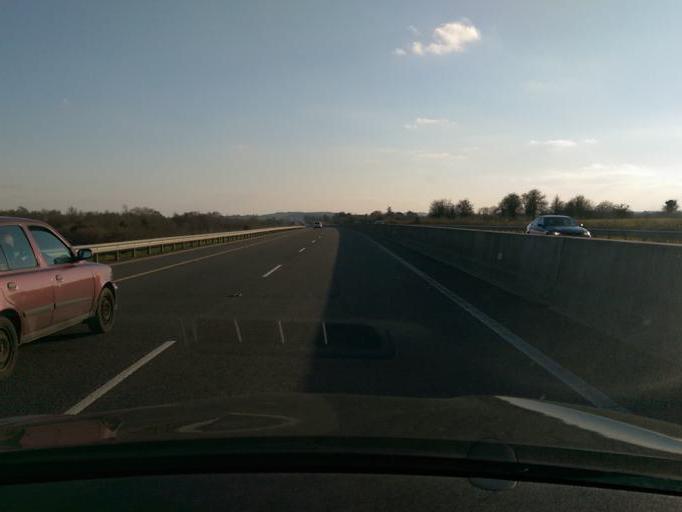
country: IE
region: Leinster
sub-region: Laois
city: Mountrath
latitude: 52.9636
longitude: -7.4383
